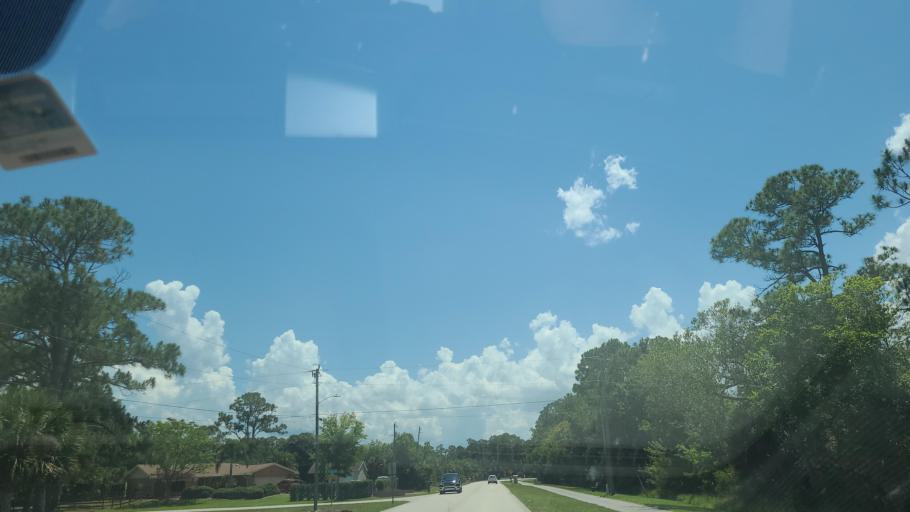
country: US
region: Florida
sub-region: Brevard County
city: Grant-Valkaria
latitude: 27.9567
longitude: -80.5697
